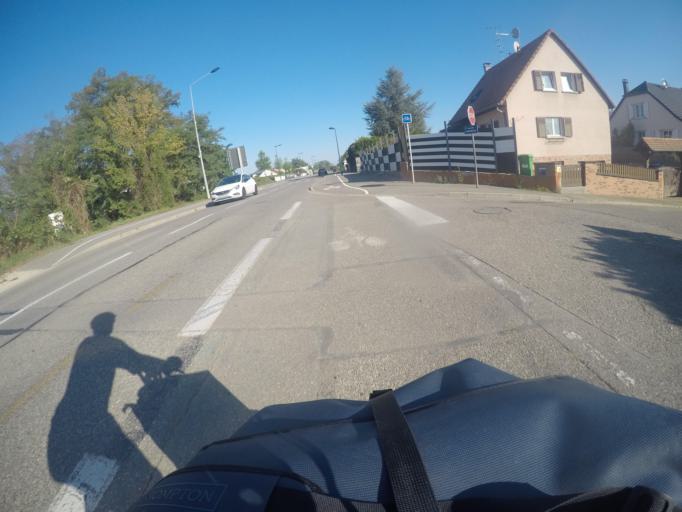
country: FR
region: Alsace
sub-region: Departement du Haut-Rhin
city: Rosenau
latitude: 47.6245
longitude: 7.5284
